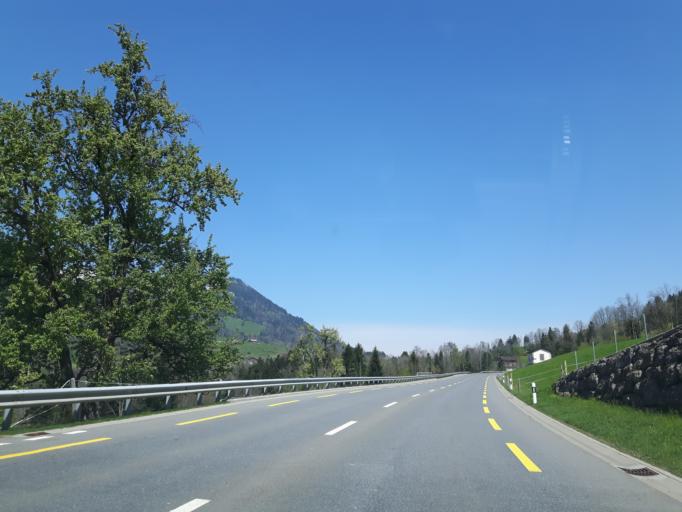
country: CH
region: Schwyz
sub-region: Bezirk Schwyz
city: Steinen
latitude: 47.0620
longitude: 8.6215
